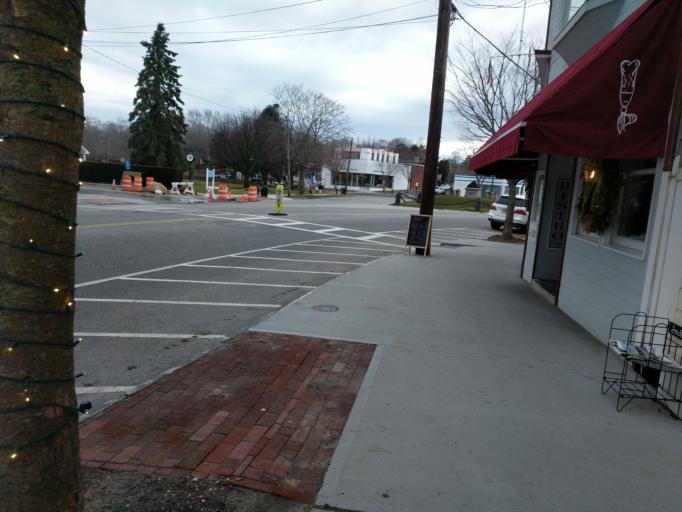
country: US
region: New York
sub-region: Suffolk County
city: Southampton
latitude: 40.8835
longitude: -72.3919
